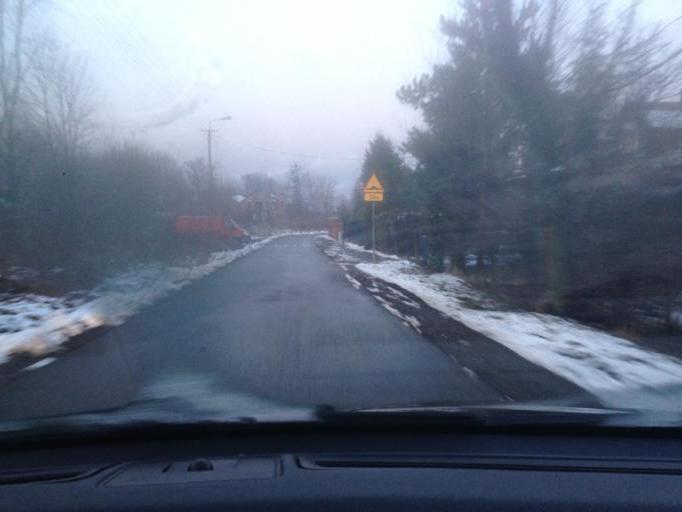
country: PL
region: Silesian Voivodeship
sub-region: Powiat bielski
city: Bystra
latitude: 49.7820
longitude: 19.0305
